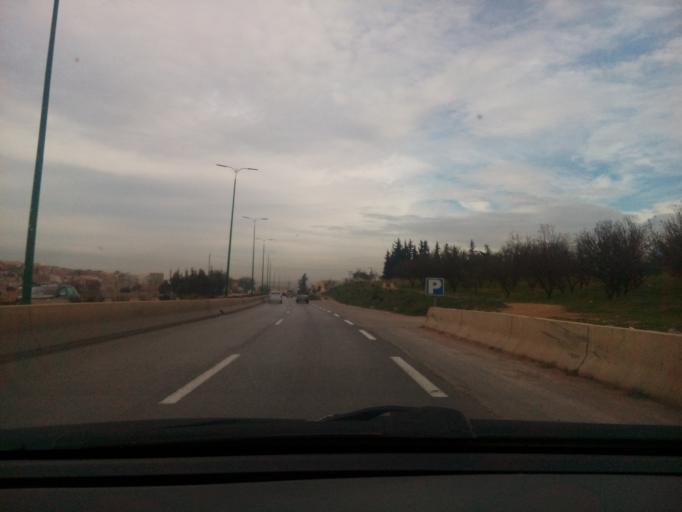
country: DZ
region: Tlemcen
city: Chetouane
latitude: 34.9119
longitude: -1.3302
